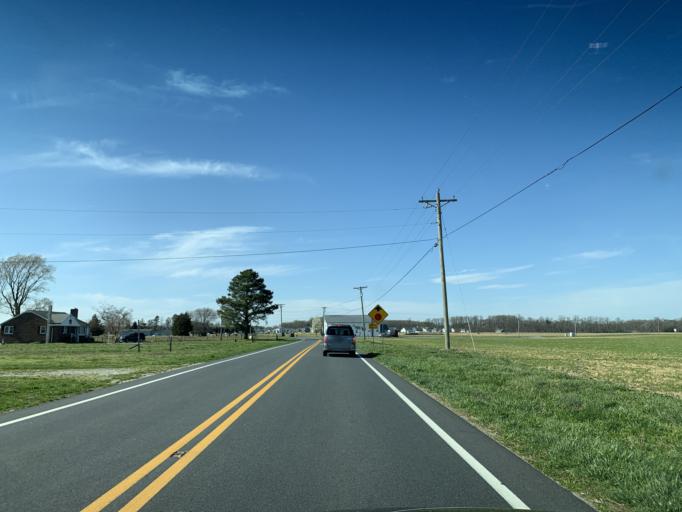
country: US
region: Delaware
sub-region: Kent County
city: Riverview
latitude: 38.9766
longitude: -75.4991
